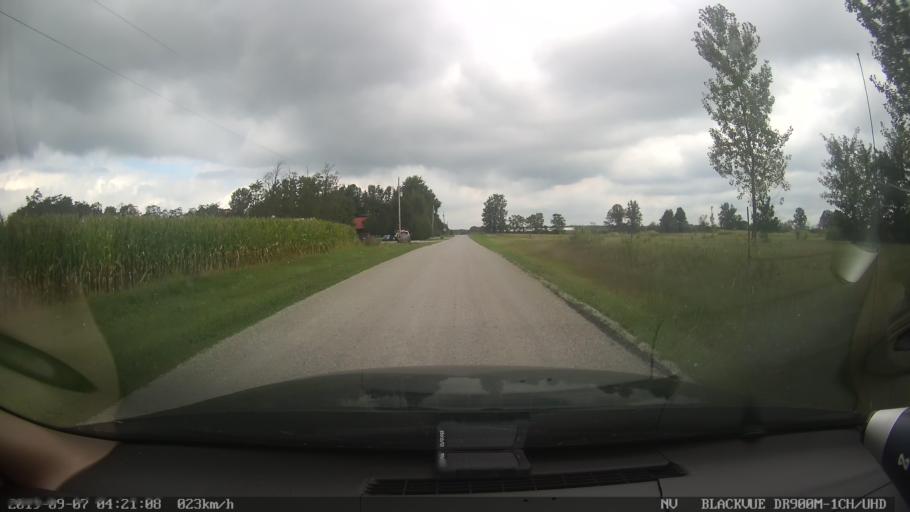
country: US
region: Ohio
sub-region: Knox County
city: Centerburg
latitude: 40.2639
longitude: -82.6721
